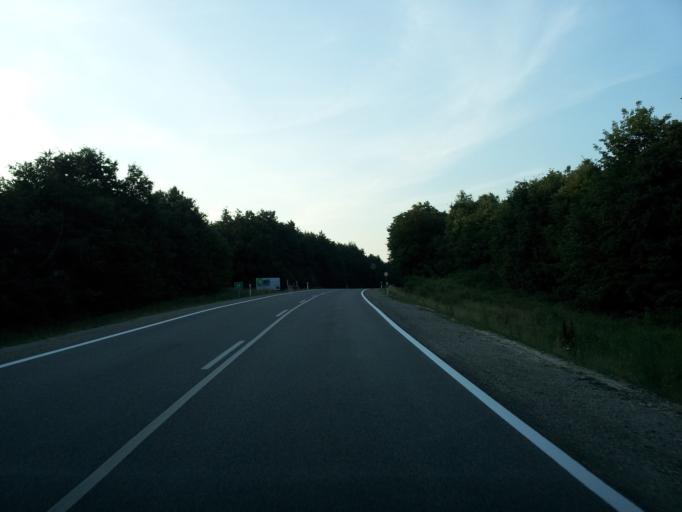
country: HU
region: Zala
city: Zalalovo
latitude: 46.7972
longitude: 16.5634
